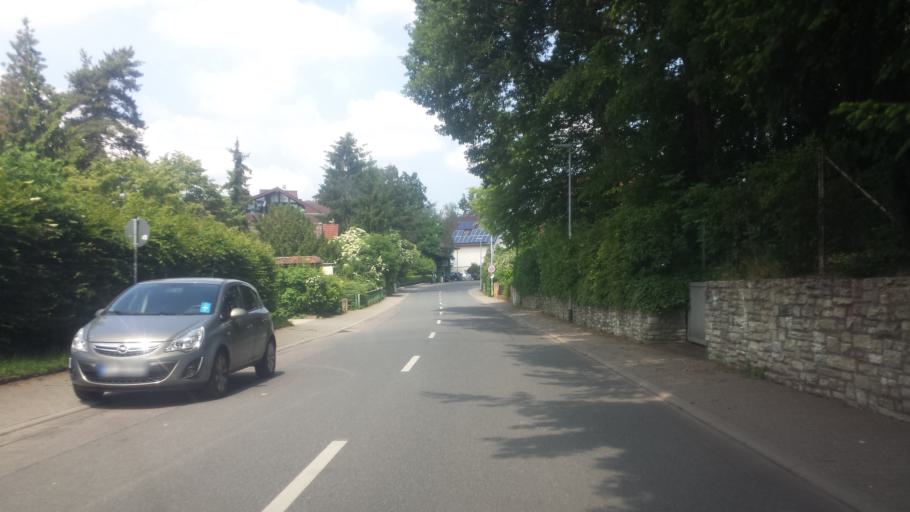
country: DE
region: Hesse
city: Dreieich
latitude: 49.9995
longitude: 8.7220
